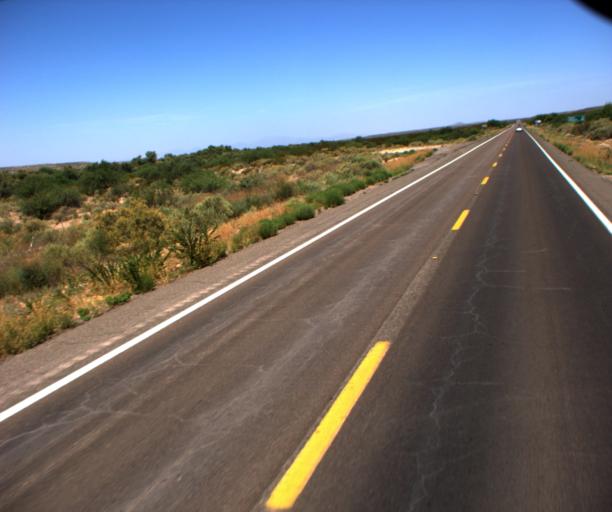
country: US
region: Arizona
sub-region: Graham County
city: Bylas
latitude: 33.1812
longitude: -110.1530
